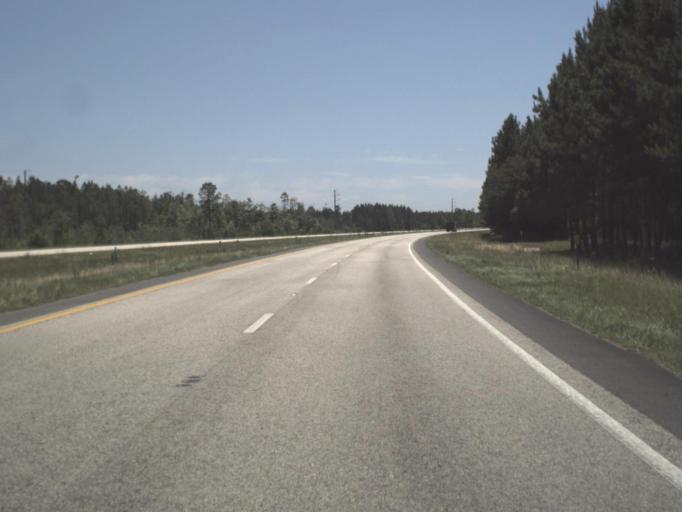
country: US
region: Florida
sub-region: Clay County
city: Bellair-Meadowbrook Terrace
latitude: 30.2203
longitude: -81.8389
